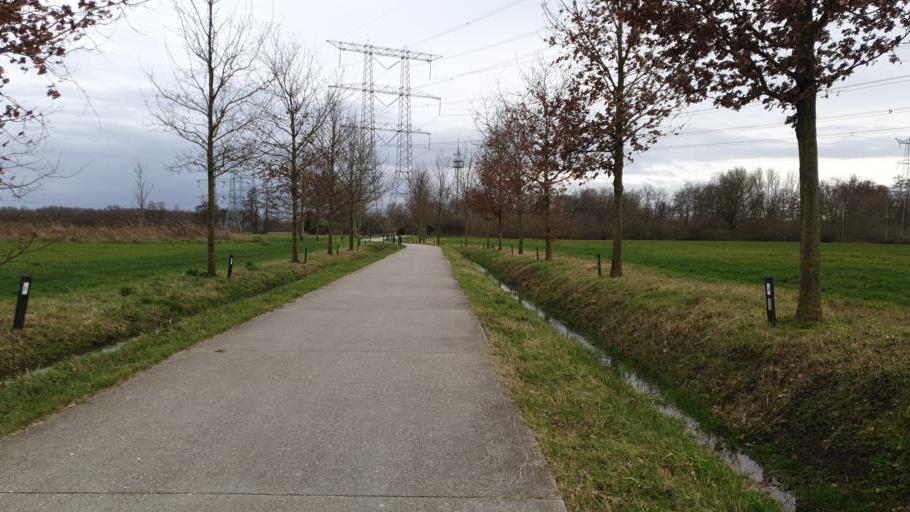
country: NL
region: North Brabant
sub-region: Gemeente Eindhoven
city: Tongelre
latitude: 51.4534
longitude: 5.5292
